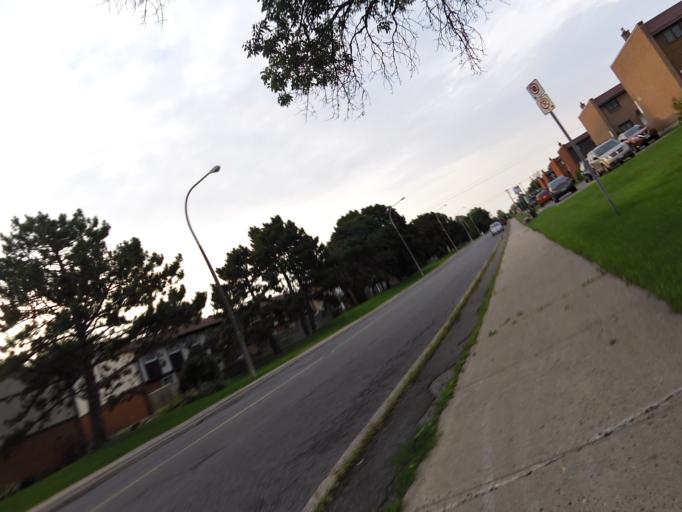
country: CA
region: Ontario
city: Bells Corners
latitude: 45.3166
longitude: -75.8275
